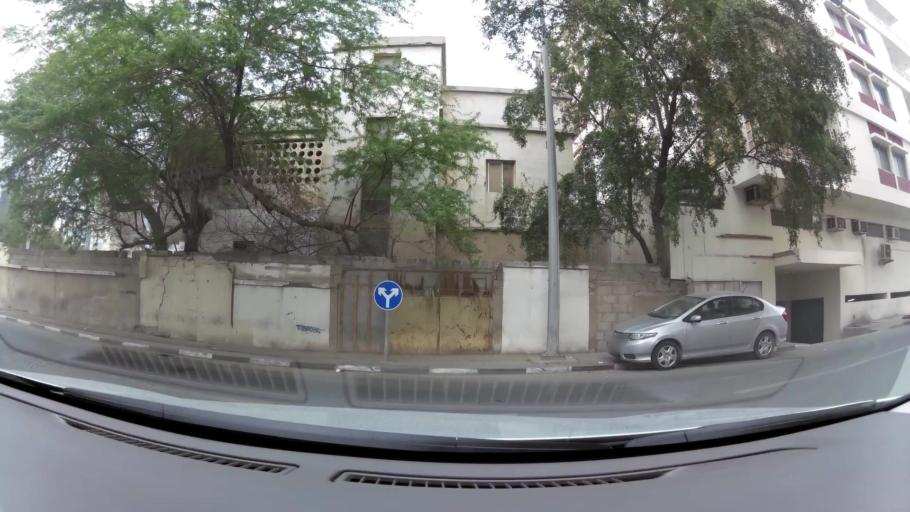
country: QA
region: Baladiyat ad Dawhah
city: Doha
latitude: 25.2756
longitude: 51.5074
